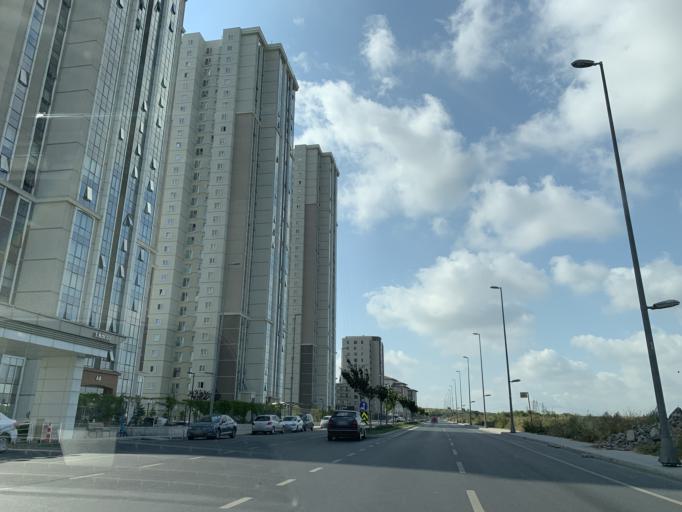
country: TR
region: Istanbul
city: Esenyurt
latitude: 41.0788
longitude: 28.6962
